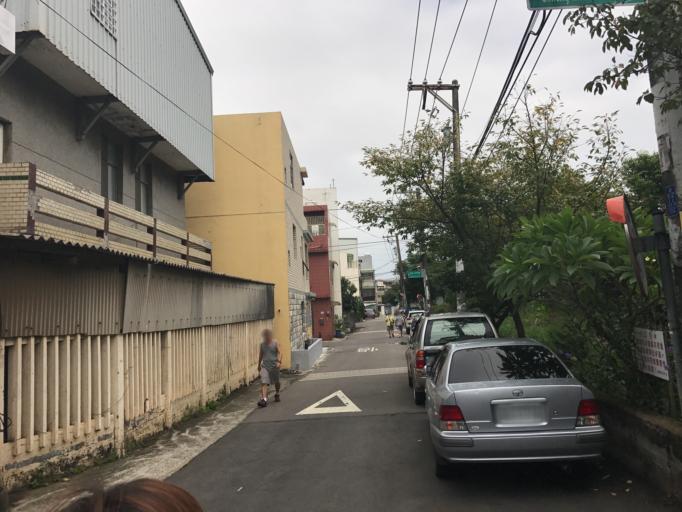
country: TW
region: Taiwan
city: Taoyuan City
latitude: 24.9483
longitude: 121.2478
